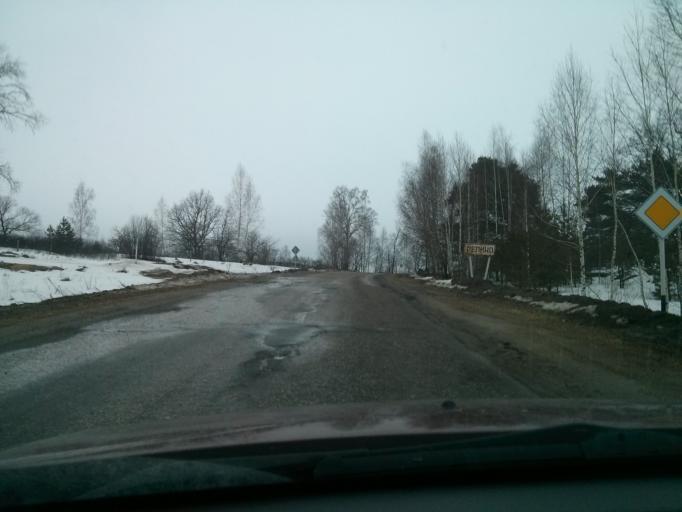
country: RU
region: Vladimir
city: Murom
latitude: 55.4601
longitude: 41.9791
